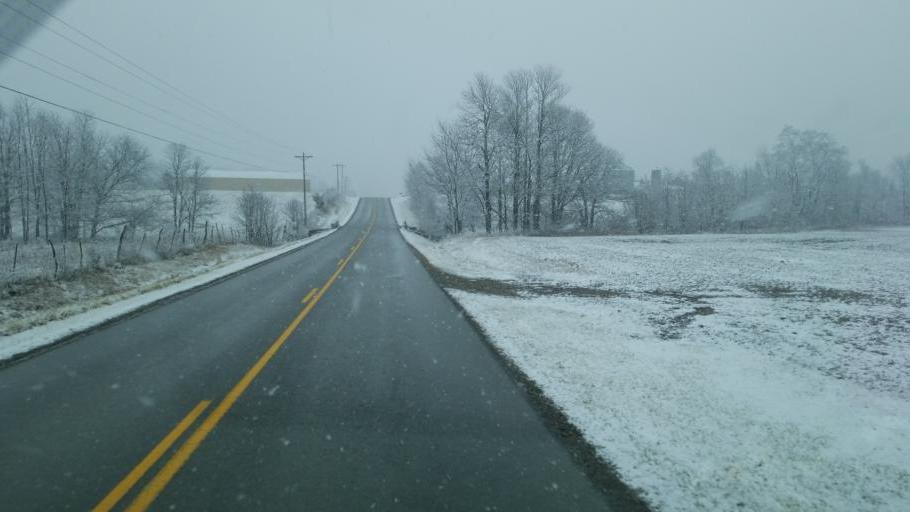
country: US
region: Ohio
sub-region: Champaign County
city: North Lewisburg
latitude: 40.3373
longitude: -83.6045
